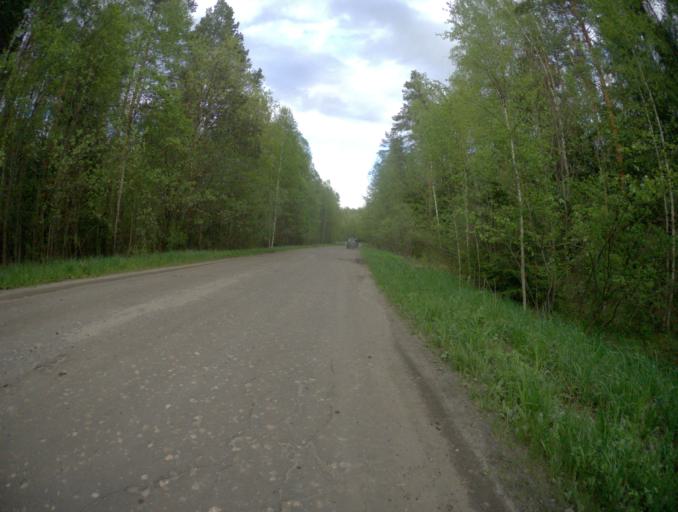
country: RU
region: Vladimir
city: Gusevskiy
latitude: 55.6953
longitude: 40.5608
